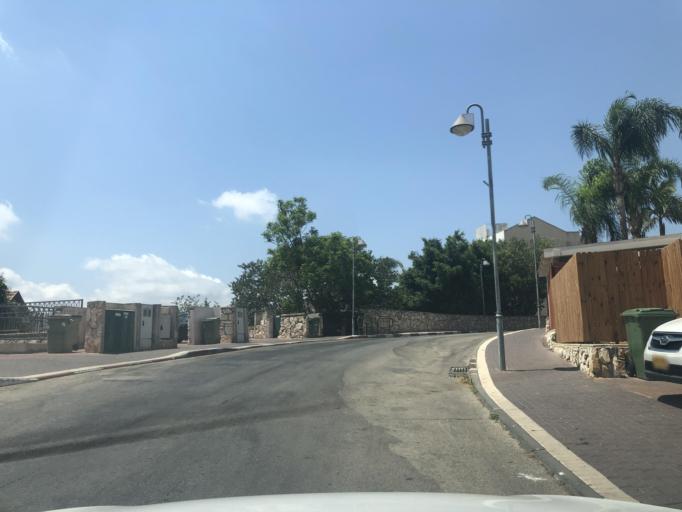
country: IL
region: Haifa
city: Daliyat el Karmil
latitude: 32.6361
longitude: 35.0880
